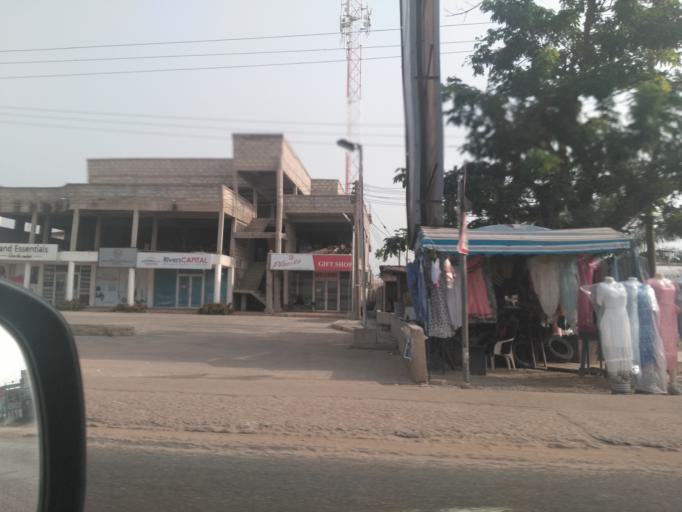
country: GH
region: Greater Accra
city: Dome
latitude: 5.6071
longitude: -0.2070
